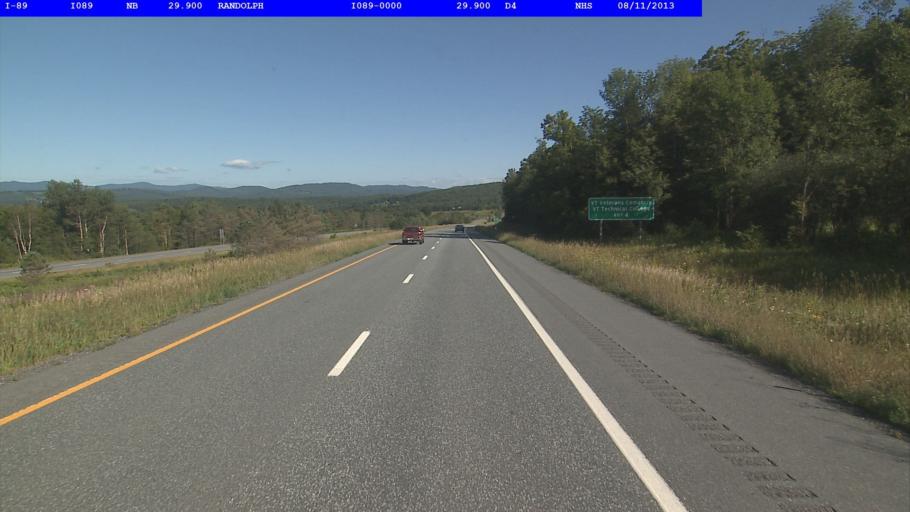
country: US
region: Vermont
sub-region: Orange County
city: Randolph
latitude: 43.9304
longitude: -72.6185
